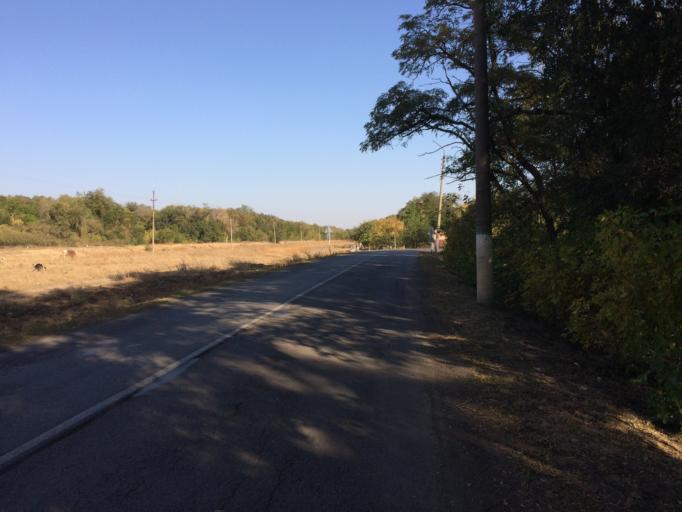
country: RU
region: Rostov
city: Gigant
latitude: 46.5277
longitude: 41.1886
